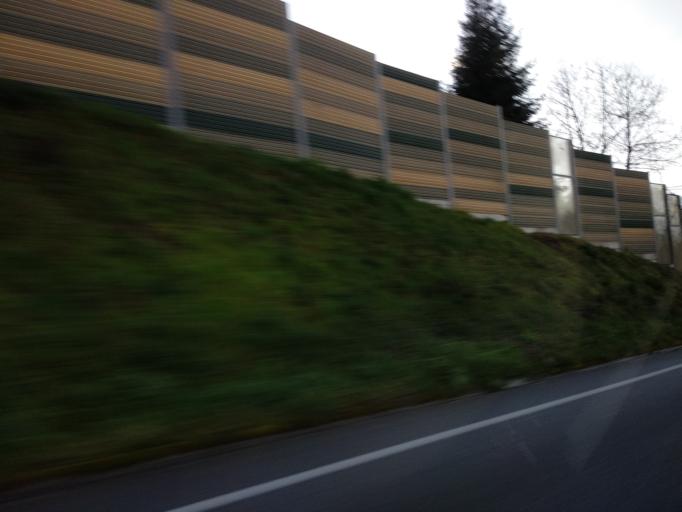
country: PT
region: Braga
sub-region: Braga
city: Oliveira
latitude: 41.4943
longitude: -8.4656
